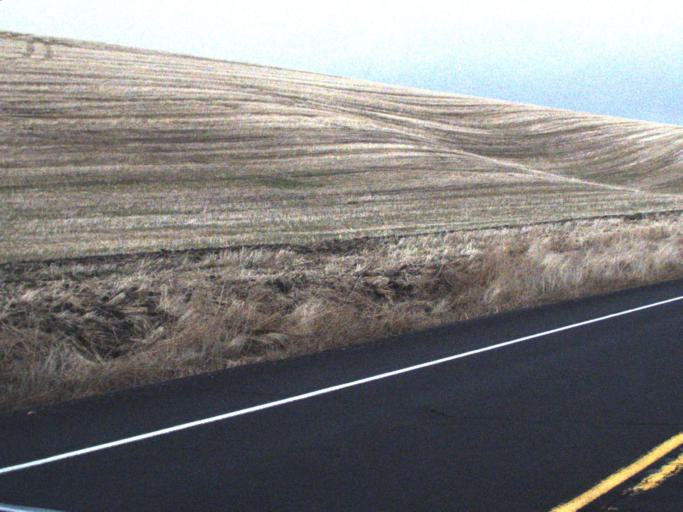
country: US
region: Washington
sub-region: Columbia County
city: Dayton
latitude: 46.3690
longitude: -117.9465
